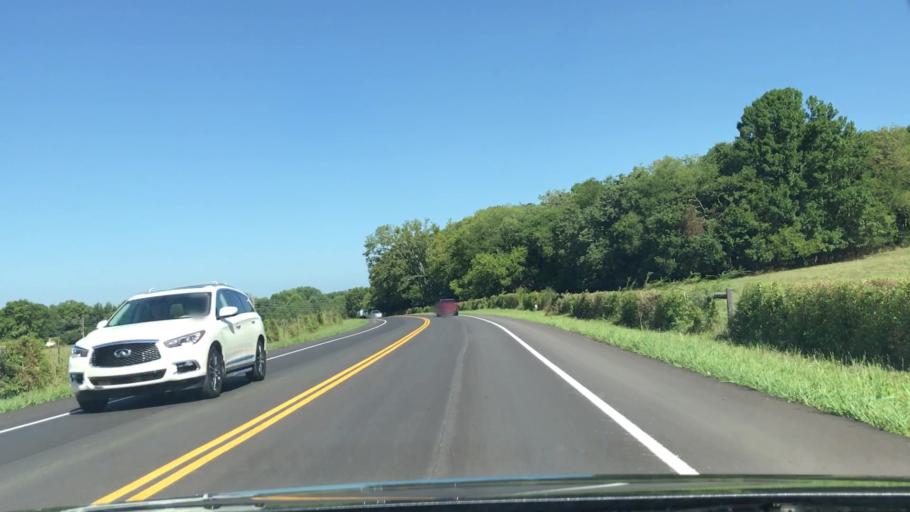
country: US
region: Tennessee
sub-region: Williamson County
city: Franklin
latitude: 35.9761
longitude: -86.8722
